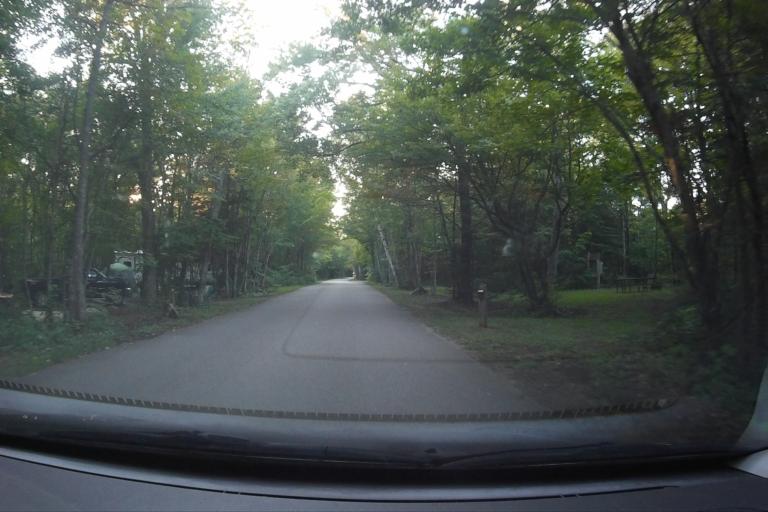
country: CA
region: Ontario
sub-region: Algoma
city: Sault Ste. Marie
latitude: 46.9689
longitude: -84.6836
